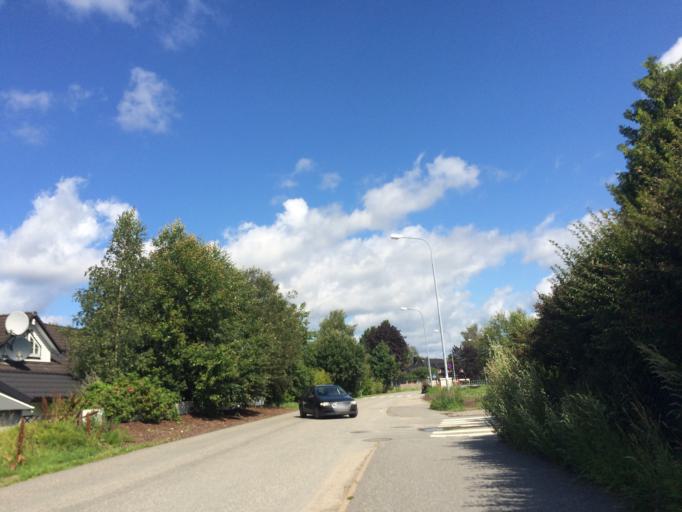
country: NO
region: Akershus
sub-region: Ski
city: Ski
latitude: 59.7165
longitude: 10.8150
